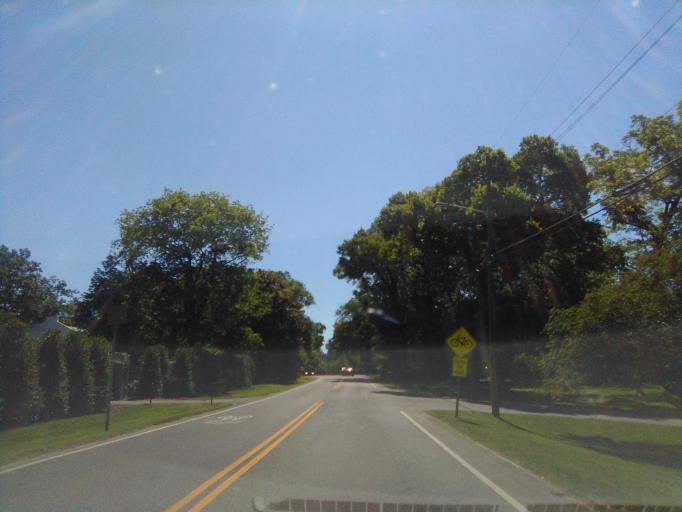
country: US
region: Tennessee
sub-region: Davidson County
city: Belle Meade
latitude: 36.1246
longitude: -86.8366
